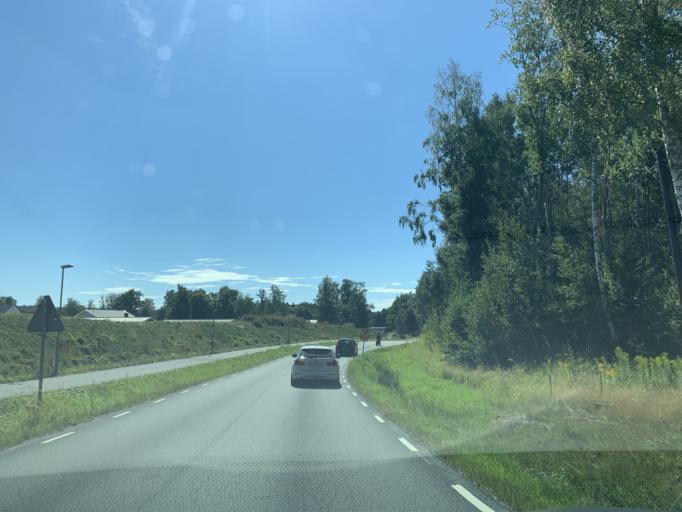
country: SE
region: Stockholm
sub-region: Ekero Kommun
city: Ekeroe
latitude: 59.2717
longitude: 17.8141
